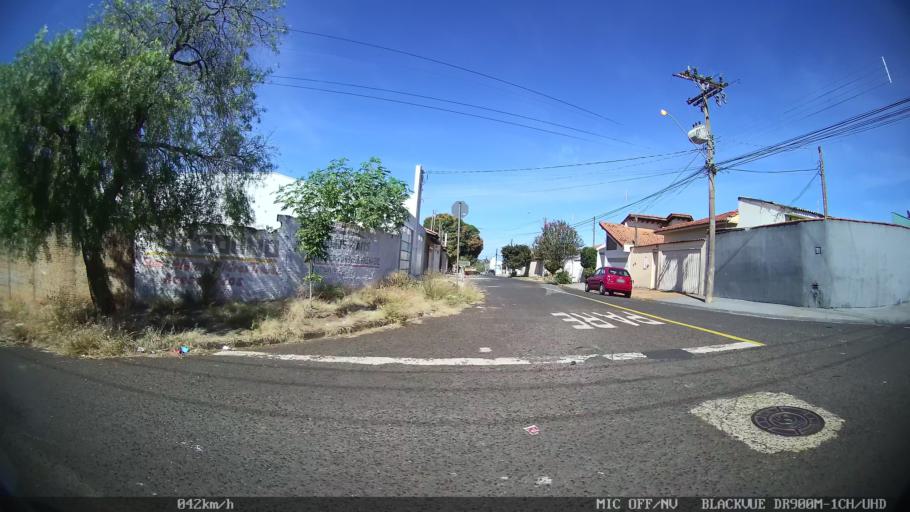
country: BR
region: Sao Paulo
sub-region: Franca
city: Franca
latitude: -20.5471
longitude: -47.3808
